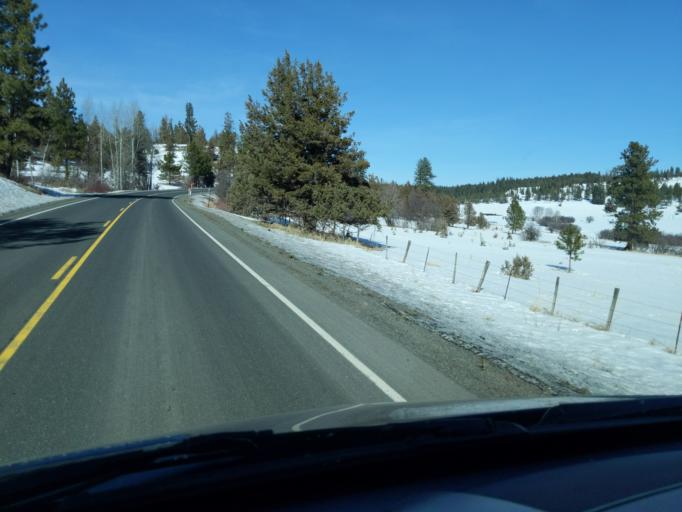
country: US
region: Oregon
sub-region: Grant County
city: John Day
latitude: 44.9020
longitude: -119.0134
